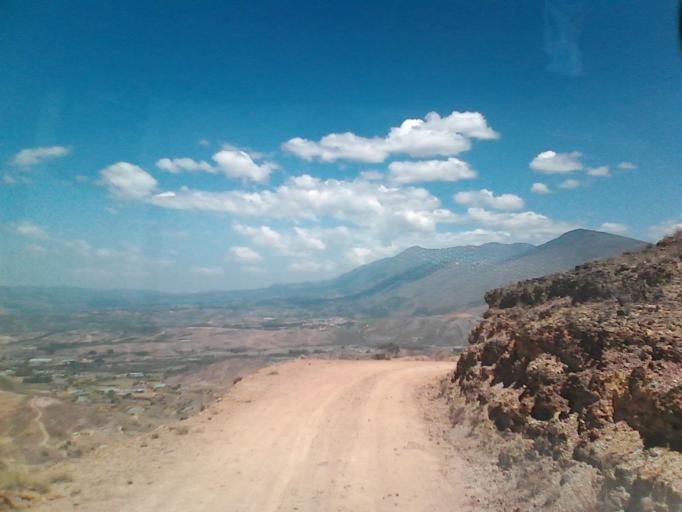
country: CO
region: Boyaca
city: Sachica
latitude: 5.5769
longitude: -73.5673
